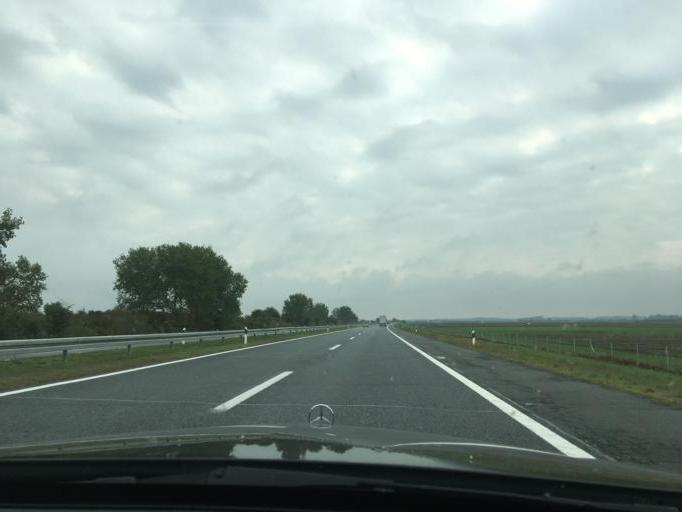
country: HR
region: Brodsko-Posavska
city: Vrbova
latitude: 45.2088
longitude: 17.5539
